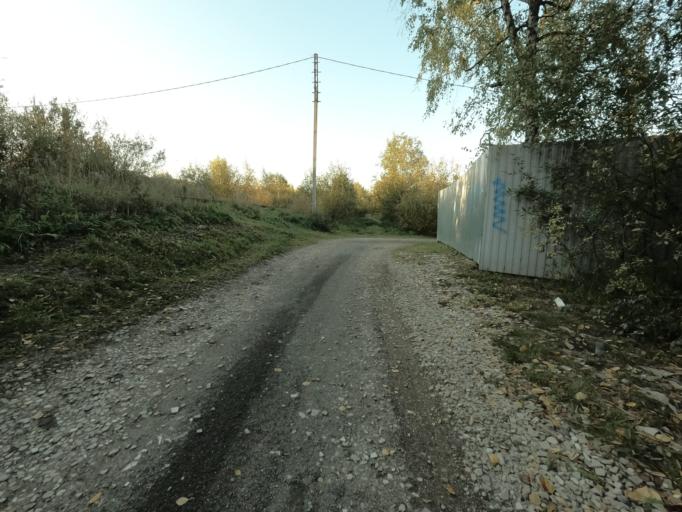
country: RU
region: Leningrad
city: Nikol'skoye
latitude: 59.7088
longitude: 30.7970
